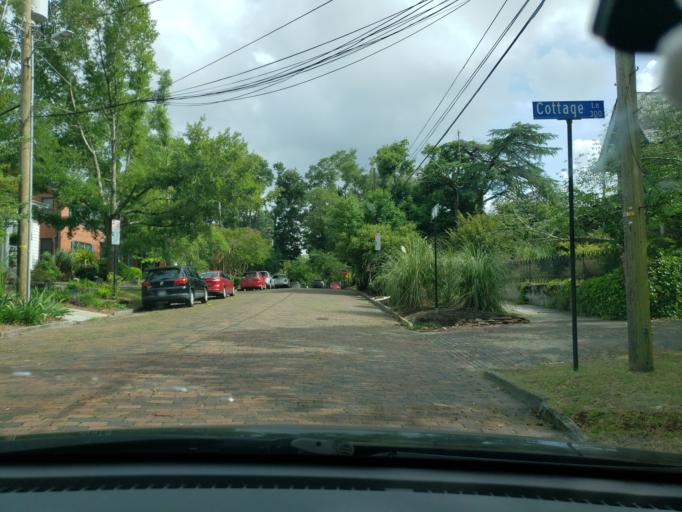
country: US
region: North Carolina
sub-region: New Hanover County
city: Wilmington
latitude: 34.2339
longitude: -77.9445
